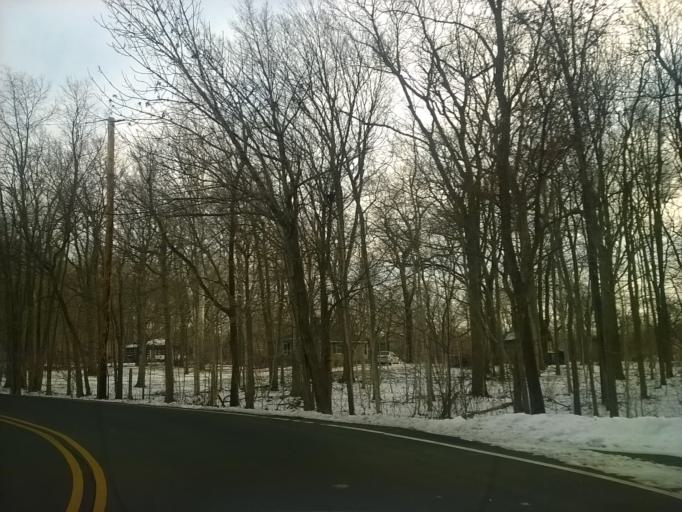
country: US
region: Indiana
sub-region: Hamilton County
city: Fishers
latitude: 39.9647
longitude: -86.0517
